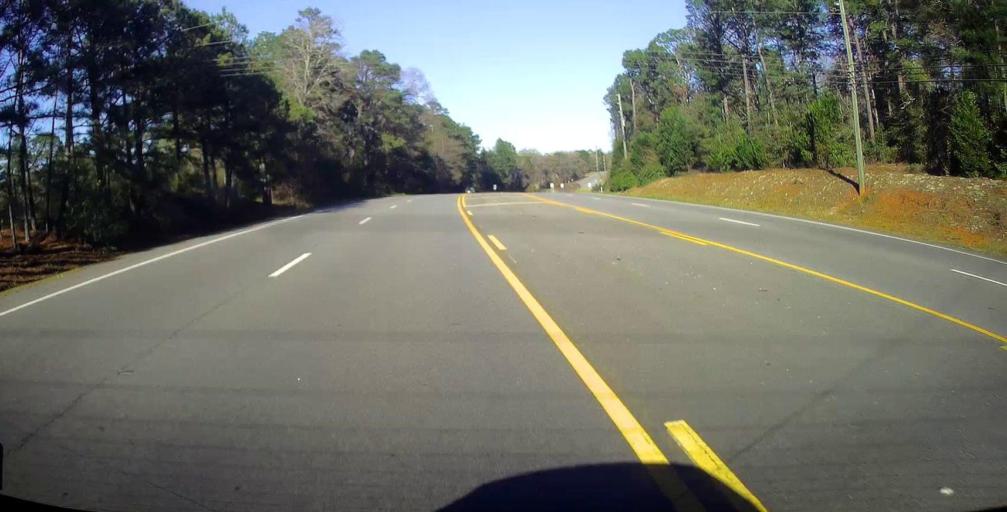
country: US
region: Georgia
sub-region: Peach County
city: Fort Valley
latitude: 32.5817
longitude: -83.8633
